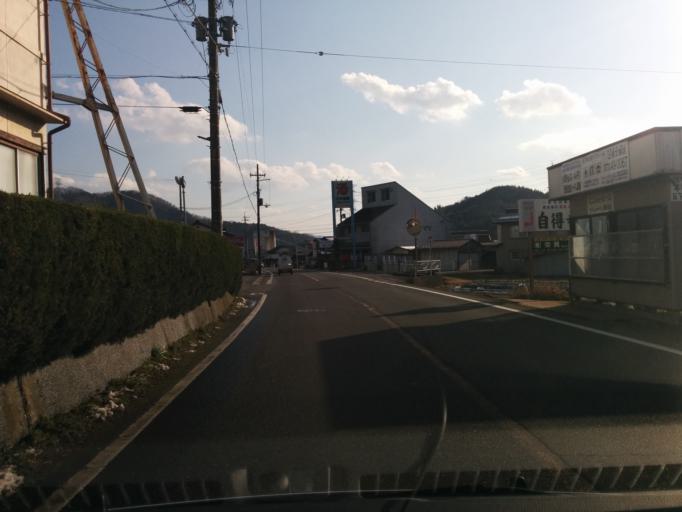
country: JP
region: Kyoto
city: Ayabe
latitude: 35.3540
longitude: 135.2211
